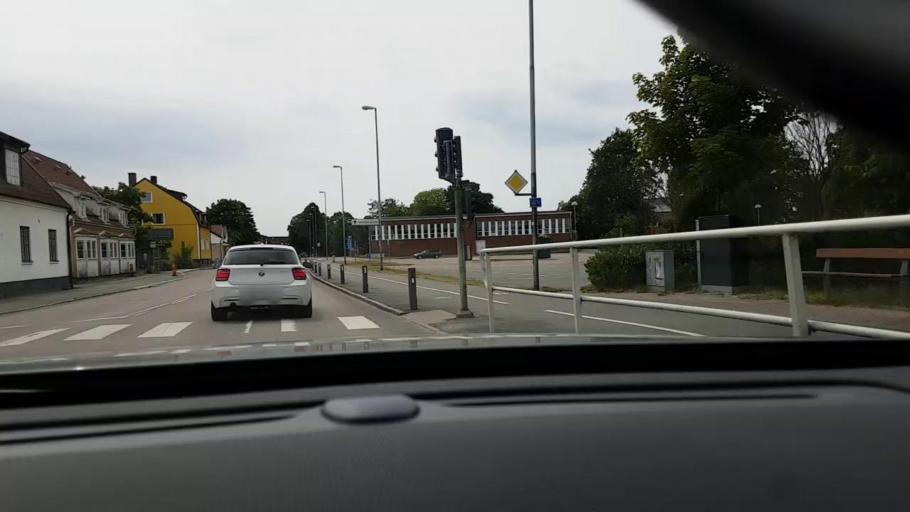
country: SE
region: Skane
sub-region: Hassleholms Kommun
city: Hassleholm
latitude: 56.1625
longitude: 13.7734
